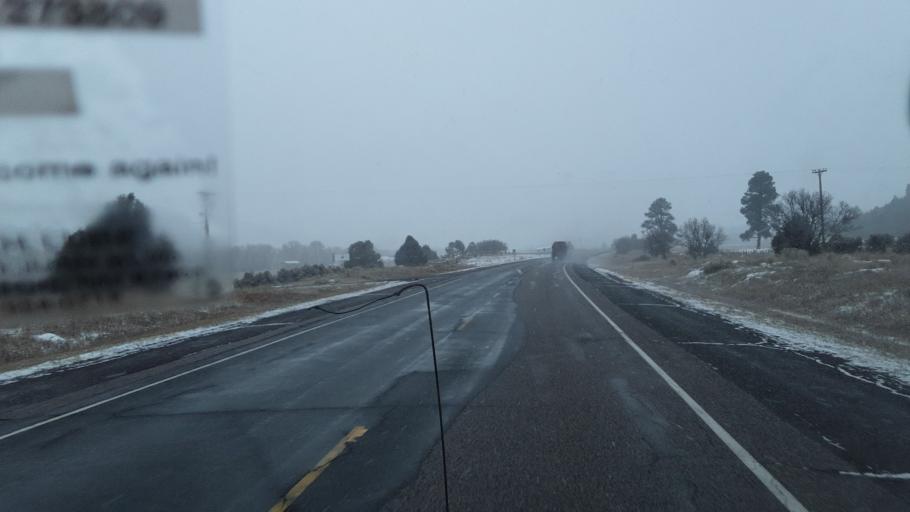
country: US
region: New Mexico
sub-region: Rio Arriba County
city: Chama
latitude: 36.8223
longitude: -106.5692
